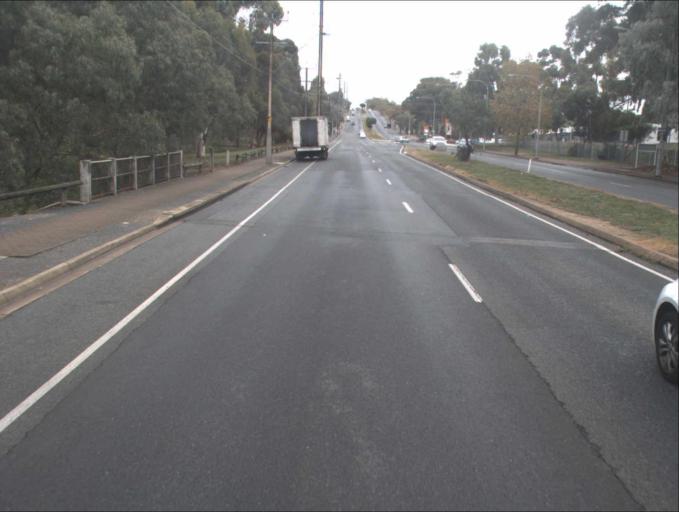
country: AU
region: South Australia
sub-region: Port Adelaide Enfield
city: Gilles Plains
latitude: -34.8453
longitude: 138.6650
